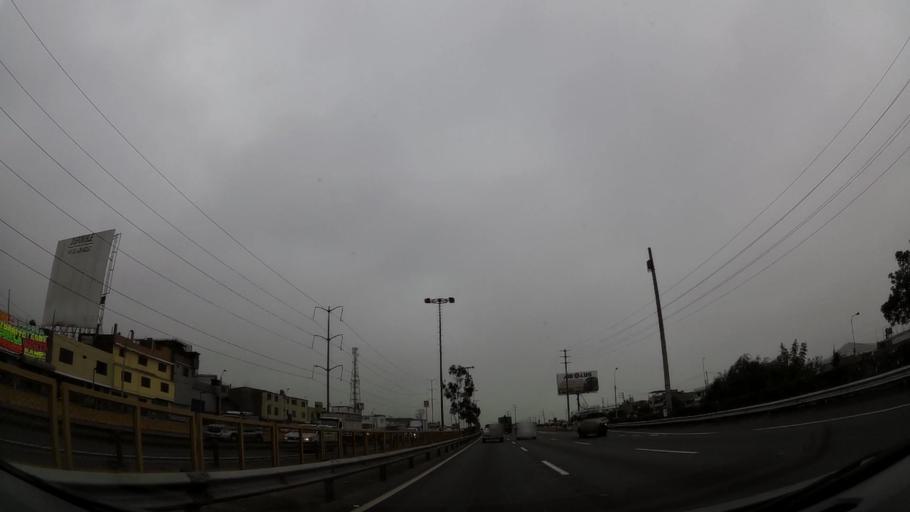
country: PE
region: Lima
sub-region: Lima
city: Surco
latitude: -12.1703
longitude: -76.9794
